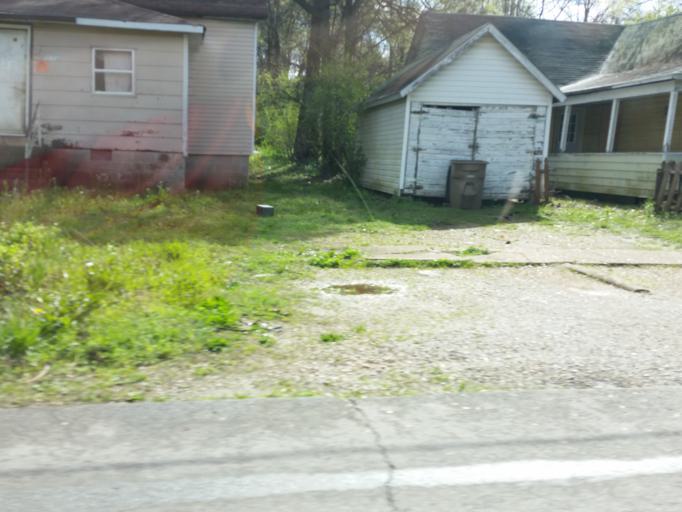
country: US
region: Missouri
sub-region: Butler County
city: Poplar Bluff
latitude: 36.7649
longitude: -90.3918
